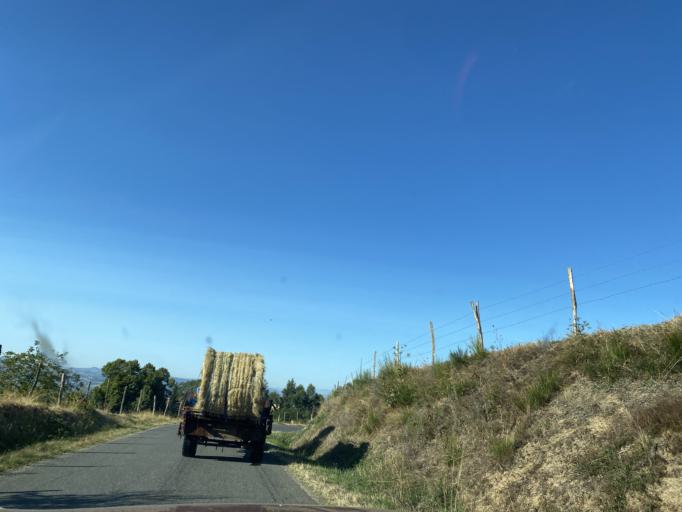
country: FR
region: Auvergne
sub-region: Departement du Puy-de-Dome
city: Escoutoux
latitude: 45.8122
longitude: 3.5870
